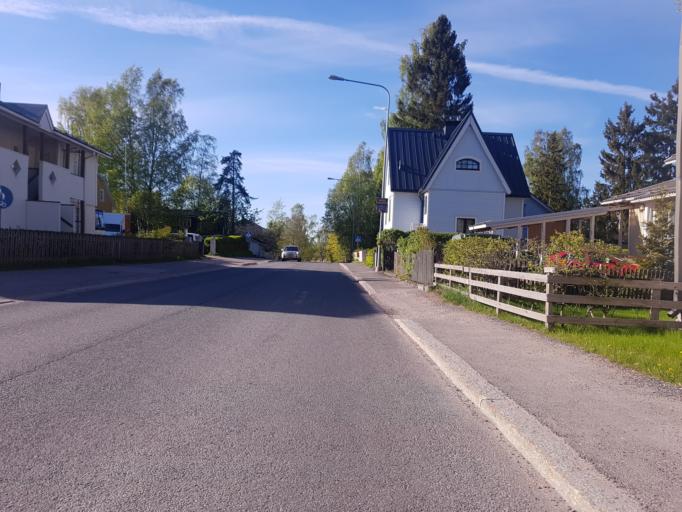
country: FI
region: Uusimaa
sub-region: Helsinki
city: Vantaa
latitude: 60.2662
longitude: 25.0251
